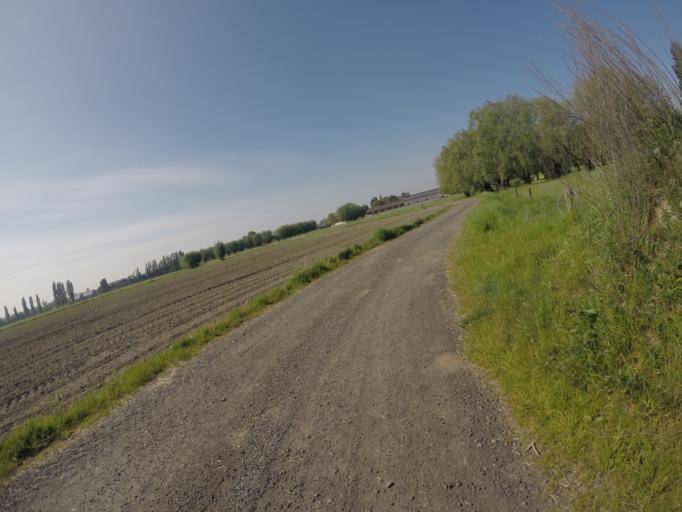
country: BE
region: Flanders
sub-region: Provincie West-Vlaanderen
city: Beernem
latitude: 51.1579
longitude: 3.3490
